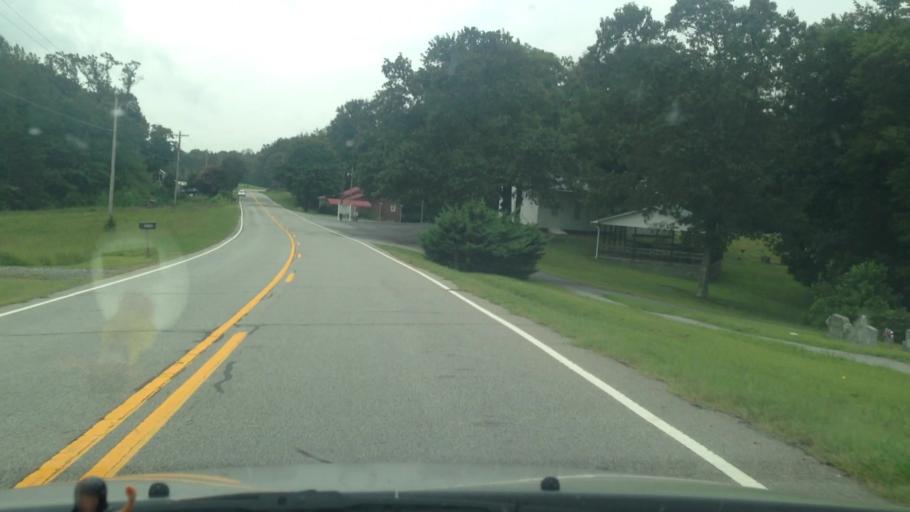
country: US
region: North Carolina
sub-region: Stokes County
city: Danbury
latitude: 36.4150
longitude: -80.1122
